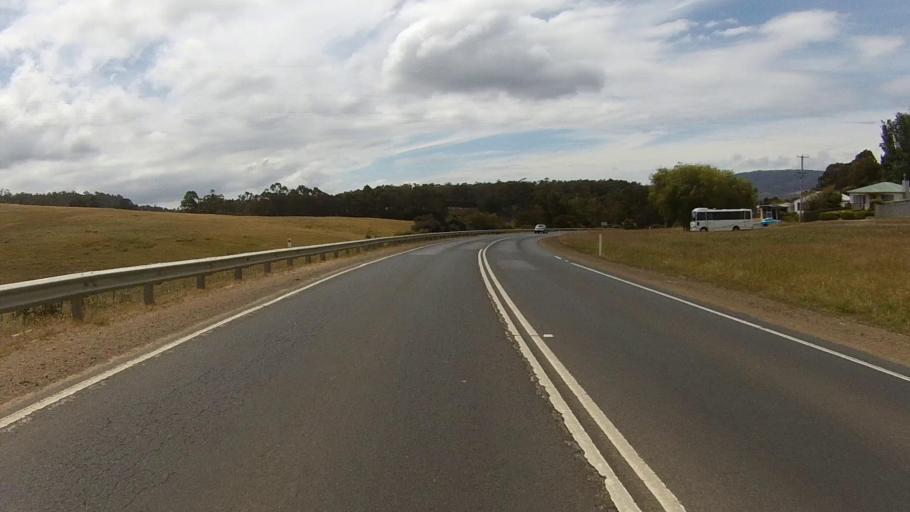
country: AU
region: Tasmania
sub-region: Kingborough
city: Margate
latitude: -43.0575
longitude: 147.2551
